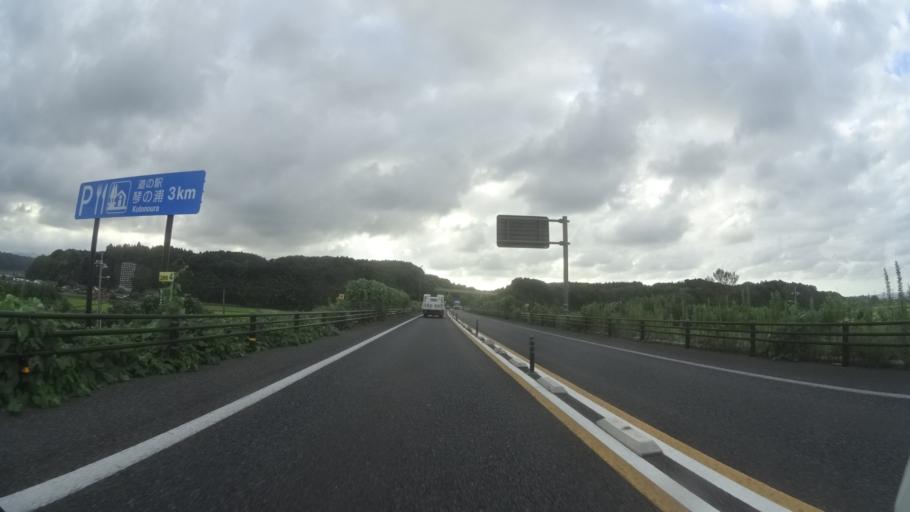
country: JP
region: Tottori
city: Kurayoshi
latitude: 35.4850
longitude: 133.6890
